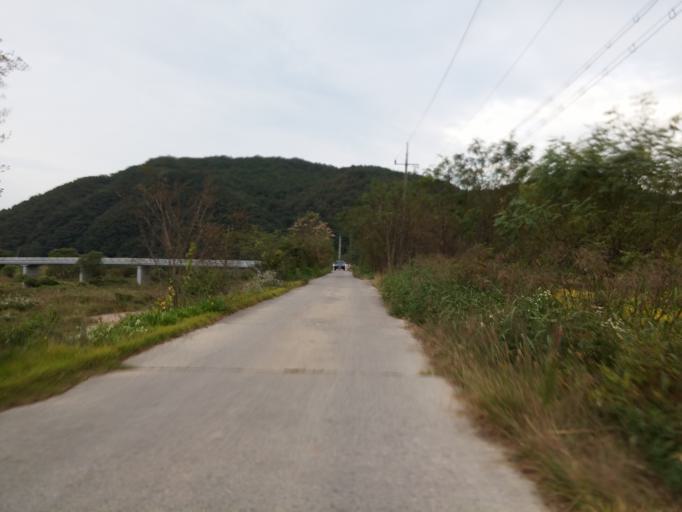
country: KR
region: Daejeon
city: Daejeon
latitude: 36.2523
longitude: 127.3240
